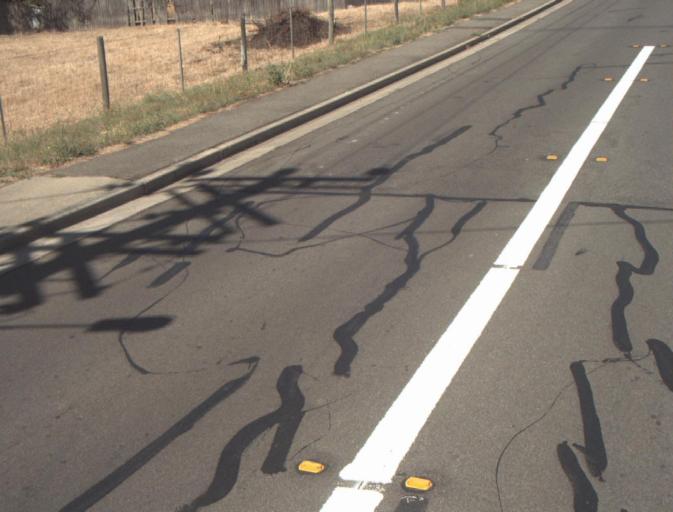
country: AU
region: Tasmania
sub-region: Launceston
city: Newstead
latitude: -41.4226
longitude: 147.1818
